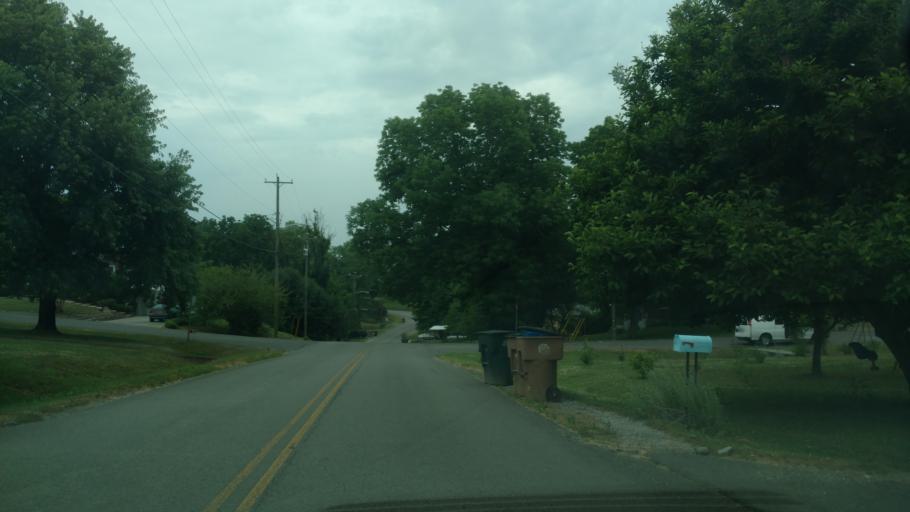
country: US
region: Tennessee
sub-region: Davidson County
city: Lakewood
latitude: 36.2046
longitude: -86.7022
